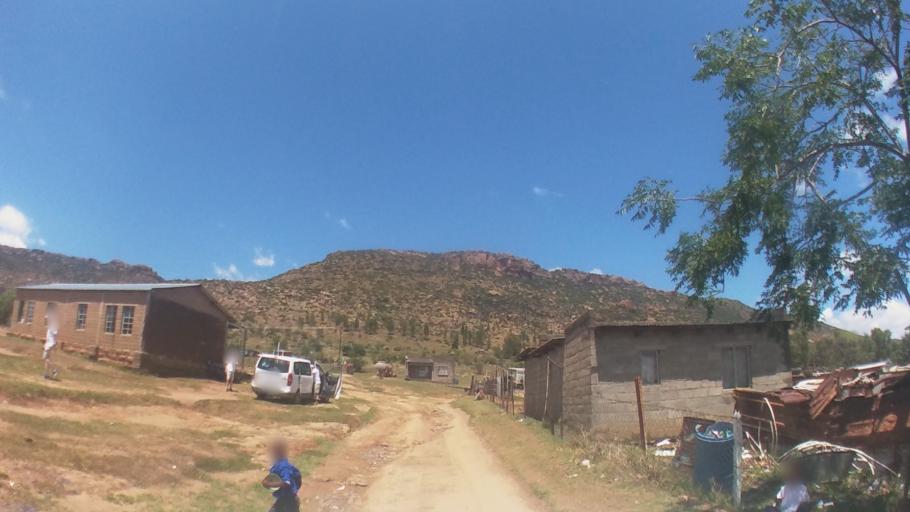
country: LS
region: Maseru
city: Maseru
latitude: -29.4403
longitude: 27.4128
